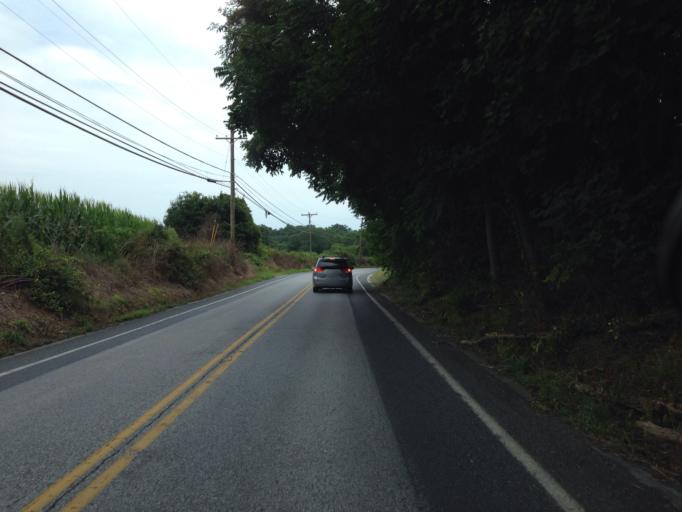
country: US
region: Delaware
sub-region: New Castle County
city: Newark
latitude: 39.7378
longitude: -75.7967
